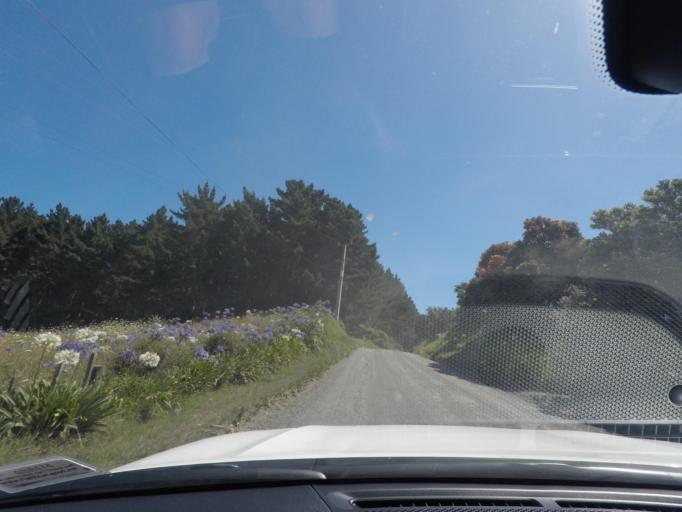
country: NZ
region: Auckland
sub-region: Auckland
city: Parakai
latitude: -36.5831
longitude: 174.2985
